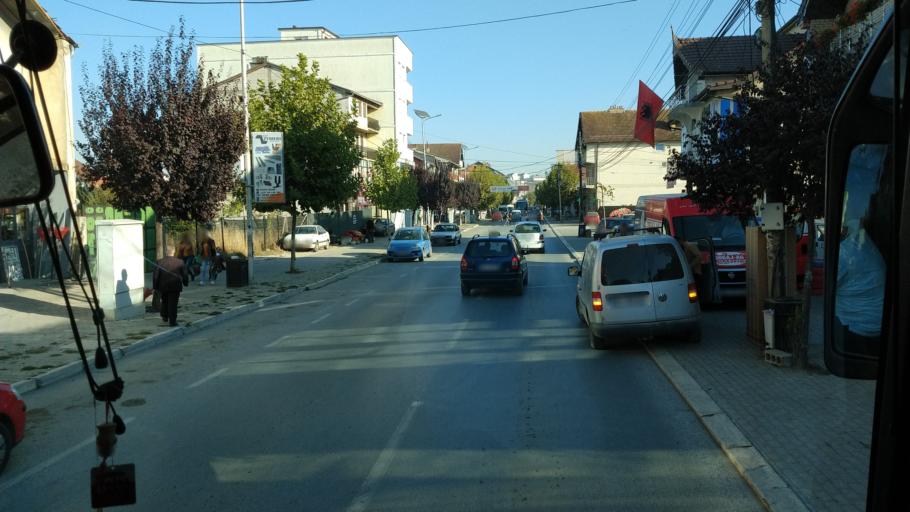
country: XK
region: Ferizaj
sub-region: Komuna e Shtimes
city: Shtime
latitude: 42.4348
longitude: 21.0346
